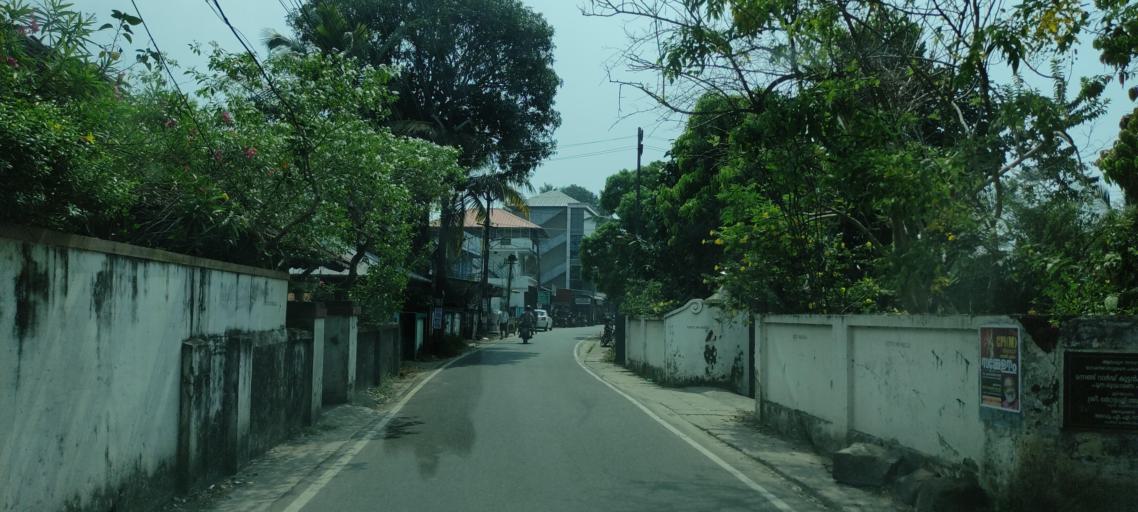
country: IN
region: Kerala
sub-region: Alappuzha
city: Alleppey
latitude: 9.5055
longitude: 76.3339
